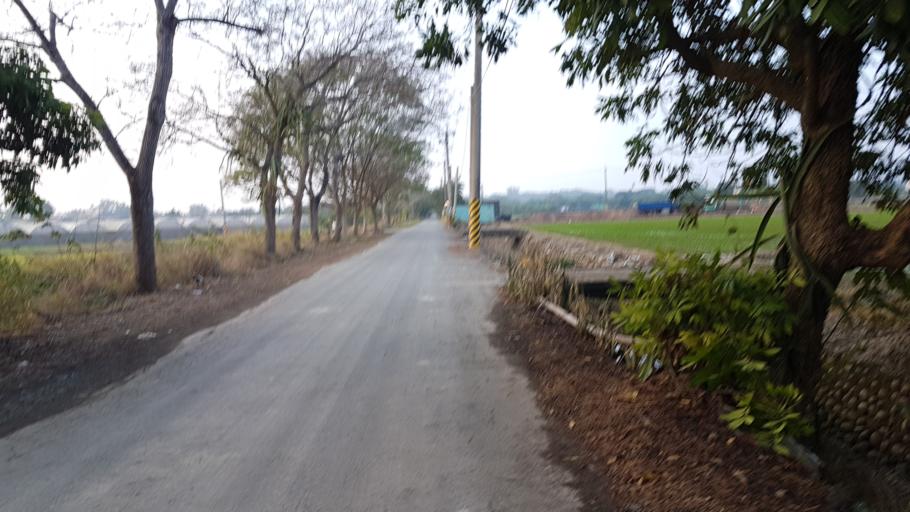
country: TW
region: Taiwan
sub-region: Chiayi
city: Jiayi Shi
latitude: 23.3758
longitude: 120.4534
